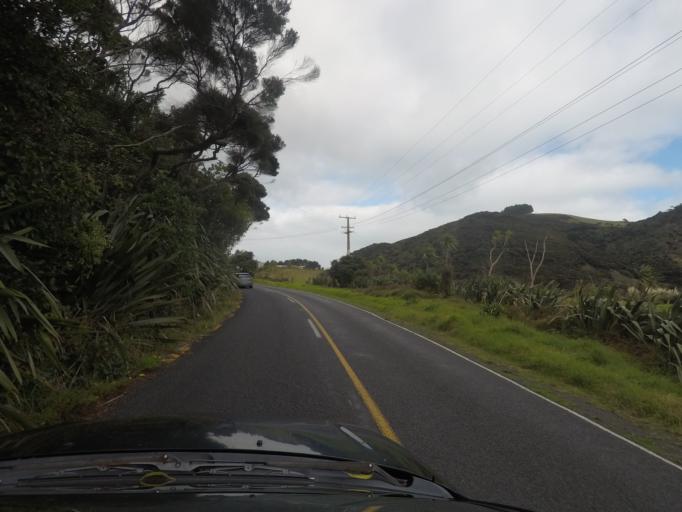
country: NZ
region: Auckland
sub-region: Auckland
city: Muriwai Beach
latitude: -36.8820
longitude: 174.4510
